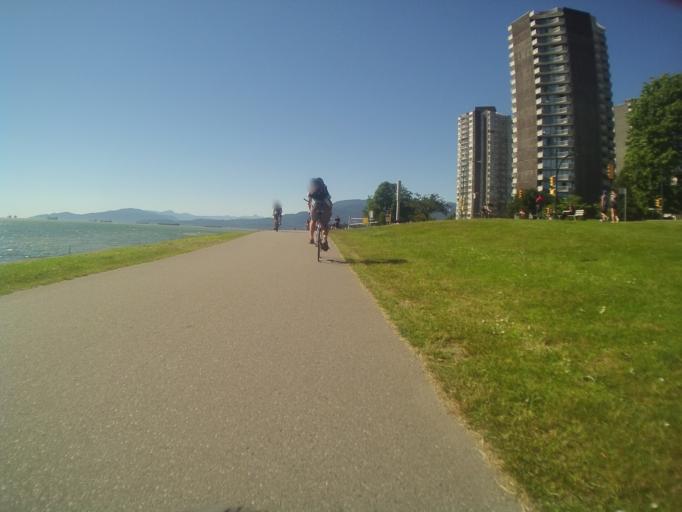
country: CA
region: British Columbia
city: West End
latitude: 49.2826
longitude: -123.1417
